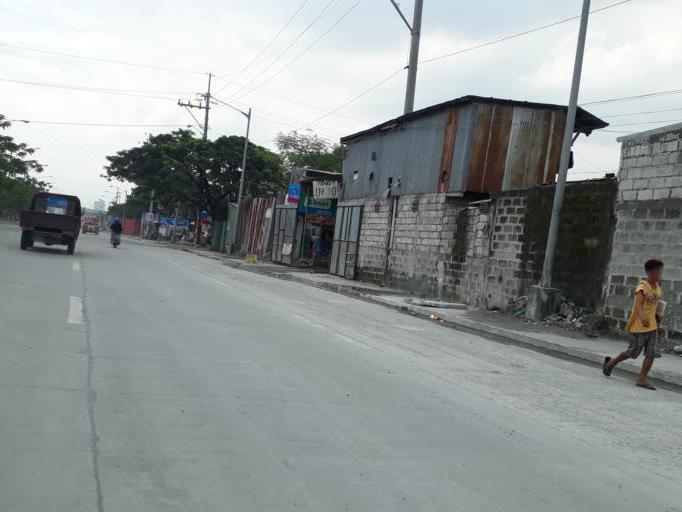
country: PH
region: Calabarzon
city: Bagong Pagasa
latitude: 14.6986
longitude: 121.0172
